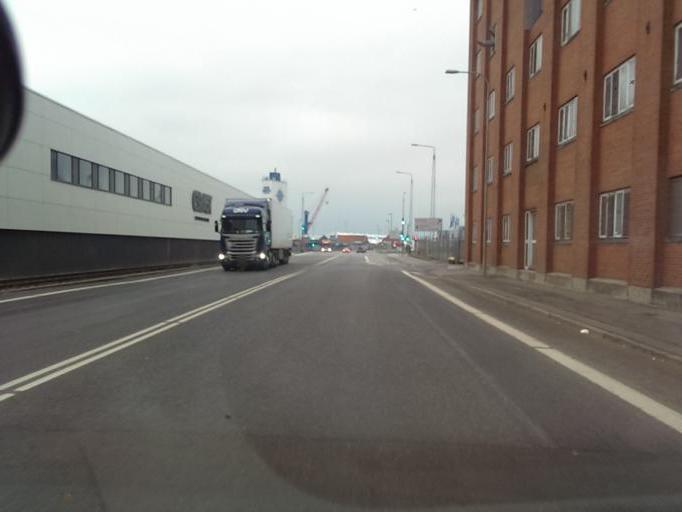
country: DK
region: South Denmark
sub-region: Esbjerg Kommune
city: Esbjerg
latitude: 55.4645
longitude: 8.4442
